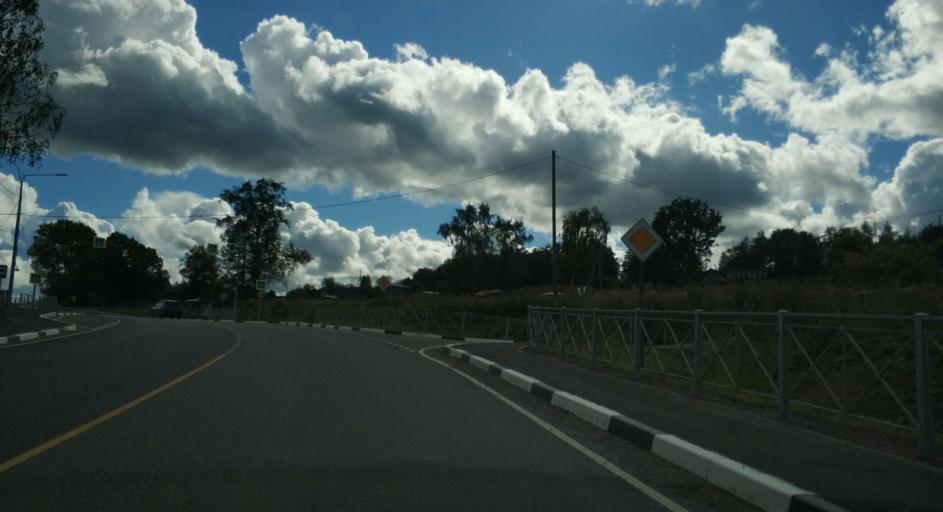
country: RU
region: Republic of Karelia
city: Ruskeala
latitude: 61.9348
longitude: 30.5909
